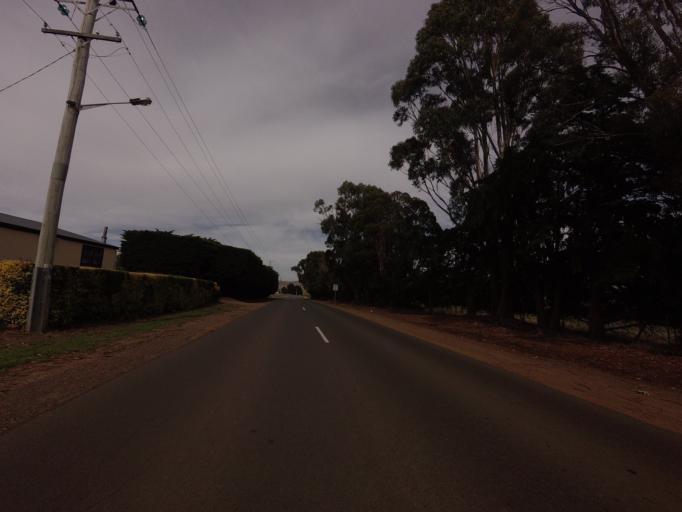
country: AU
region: Tasmania
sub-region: Brighton
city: Bridgewater
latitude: -42.3050
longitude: 147.3638
